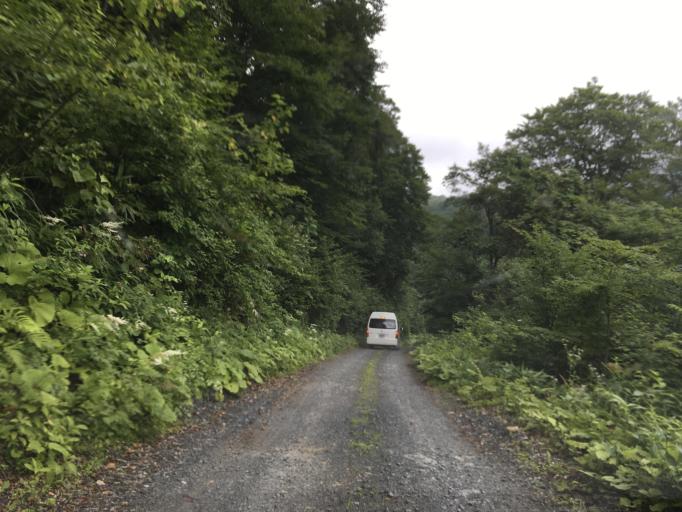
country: JP
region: Iwate
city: Ichinoseki
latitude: 38.9595
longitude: 140.8466
